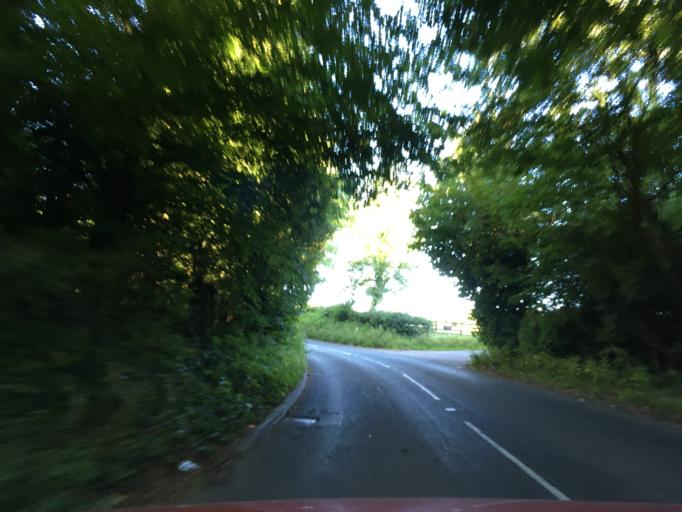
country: GB
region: Wales
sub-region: Monmouthshire
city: Chepstow
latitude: 51.6483
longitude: -2.6938
